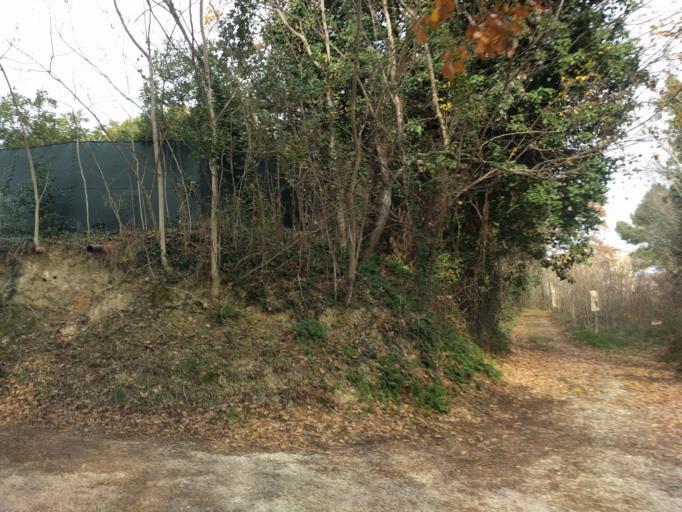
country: IT
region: The Marches
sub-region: Provincia di Pesaro e Urbino
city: Centinarola
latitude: 43.8419
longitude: 12.9921
